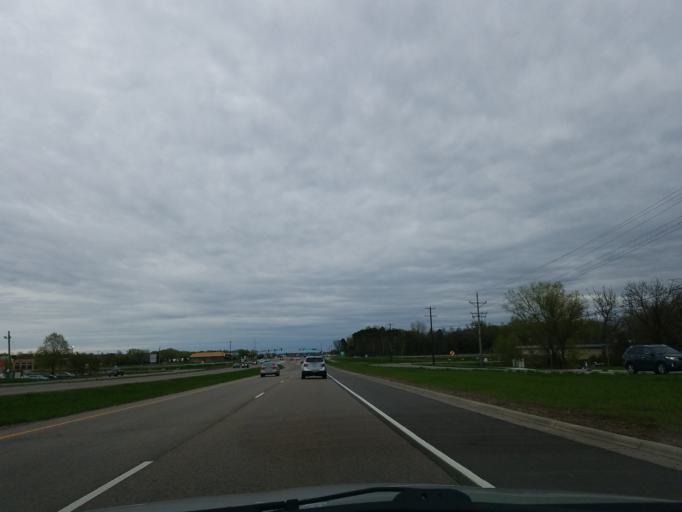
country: US
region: Minnesota
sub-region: Washington County
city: Stillwater
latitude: 45.0359
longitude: -92.8256
